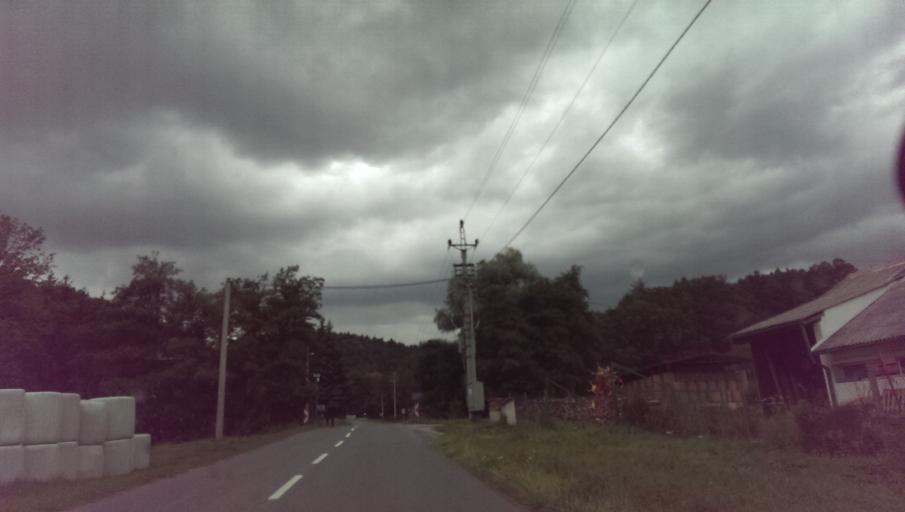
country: CZ
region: South Moravian
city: Velka nad Velickou
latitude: 48.8934
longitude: 17.5758
